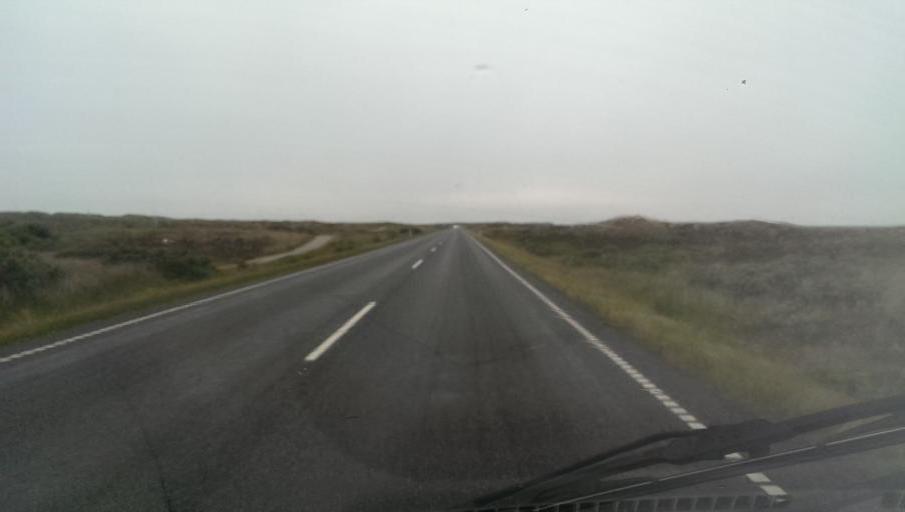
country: DK
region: Central Jutland
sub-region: Ringkobing-Skjern Kommune
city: Hvide Sande
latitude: 55.8333
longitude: 8.1728
